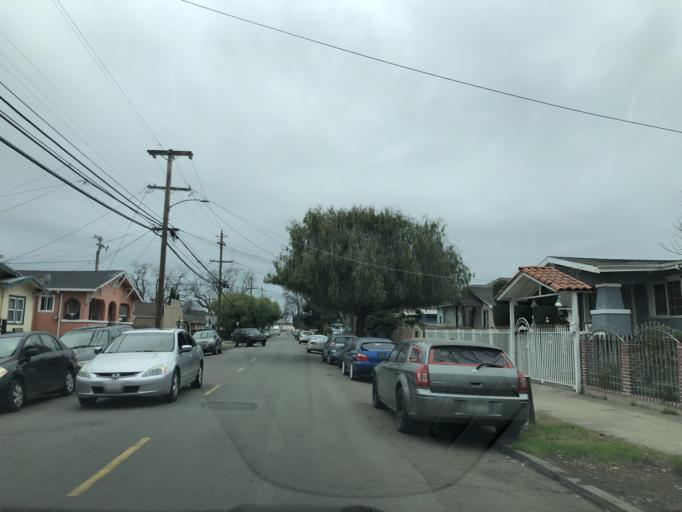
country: US
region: California
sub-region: Alameda County
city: San Leandro
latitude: 37.7460
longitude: -122.1791
